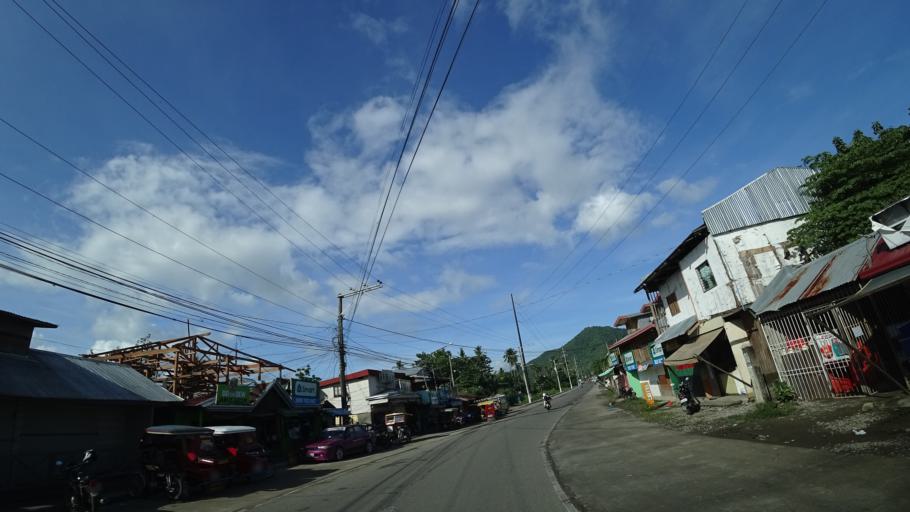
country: PH
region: Eastern Visayas
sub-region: Province of Leyte
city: Panalanoy
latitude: 11.2284
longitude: 124.9983
